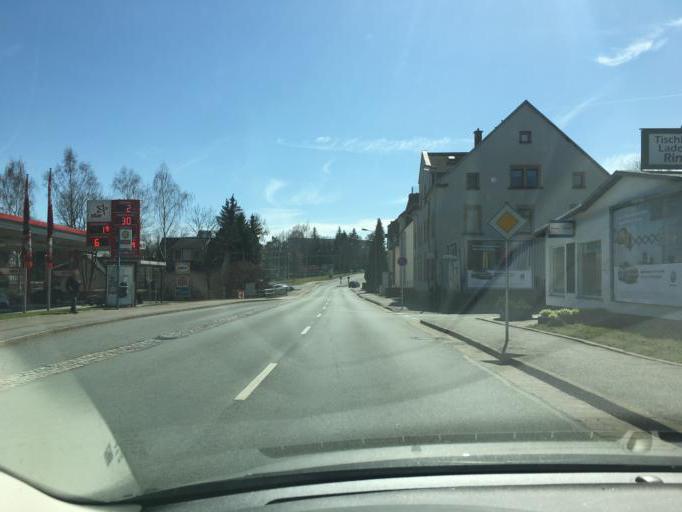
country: DE
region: Saxony
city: Neukirchen
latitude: 50.8013
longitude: 12.8986
